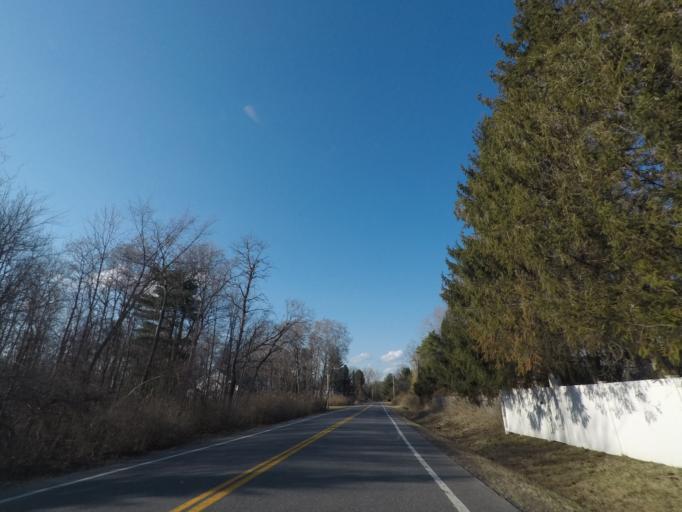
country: US
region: New York
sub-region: Schenectady County
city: Niskayuna
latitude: 42.8213
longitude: -73.7909
